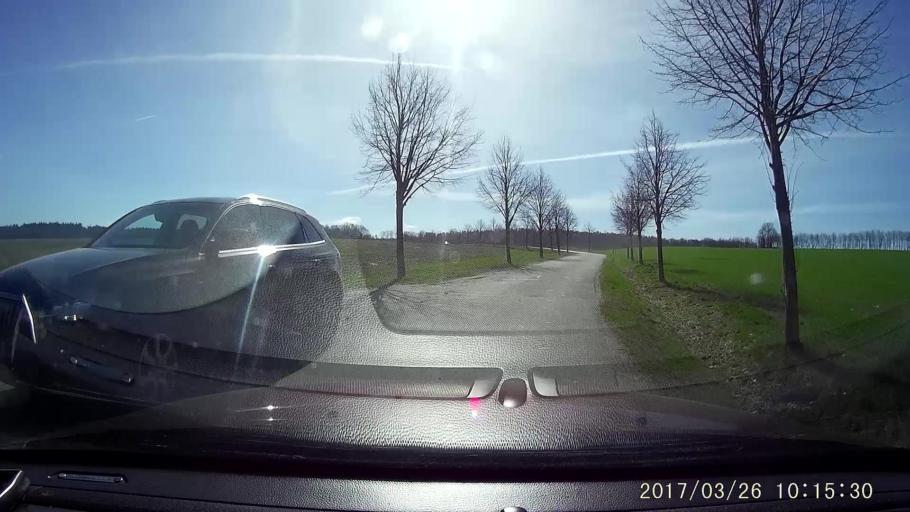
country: DE
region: Saxony
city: Herrnhut
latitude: 51.0699
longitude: 14.7462
